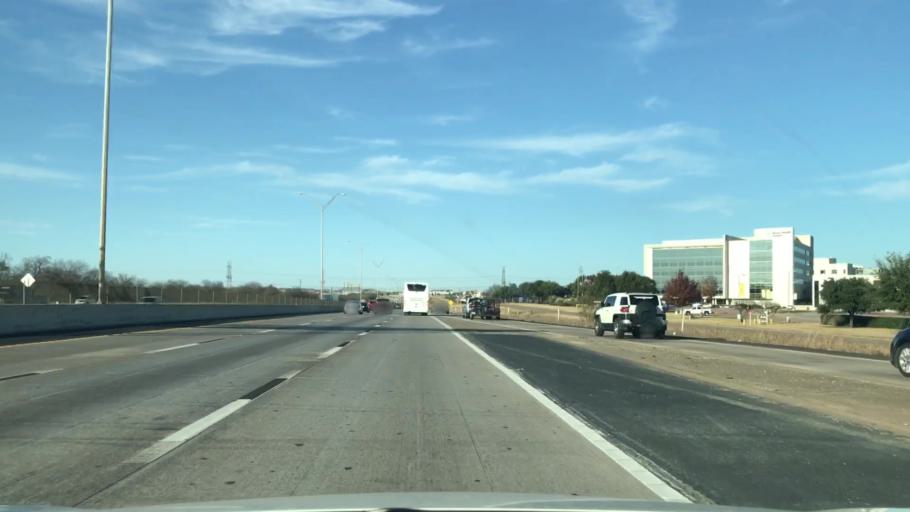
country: US
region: Texas
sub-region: Johnson County
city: Burleson
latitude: 32.5831
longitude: -97.3195
